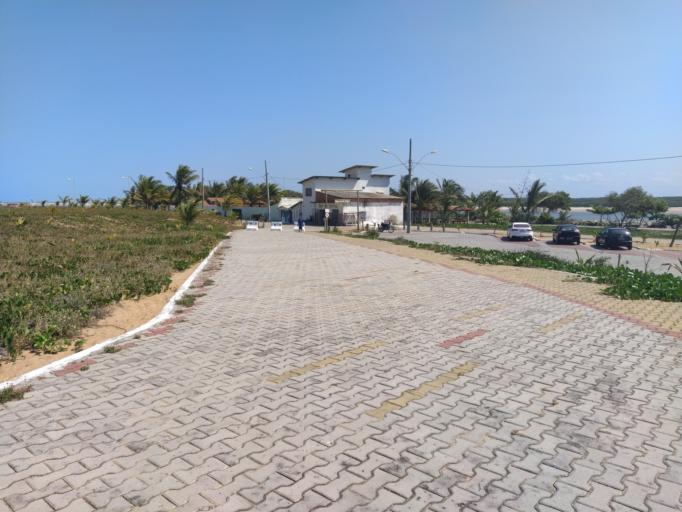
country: BR
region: Espirito Santo
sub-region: Conceicao Da Barra
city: Conceicao da Barra
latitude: -18.5985
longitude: -39.7284
